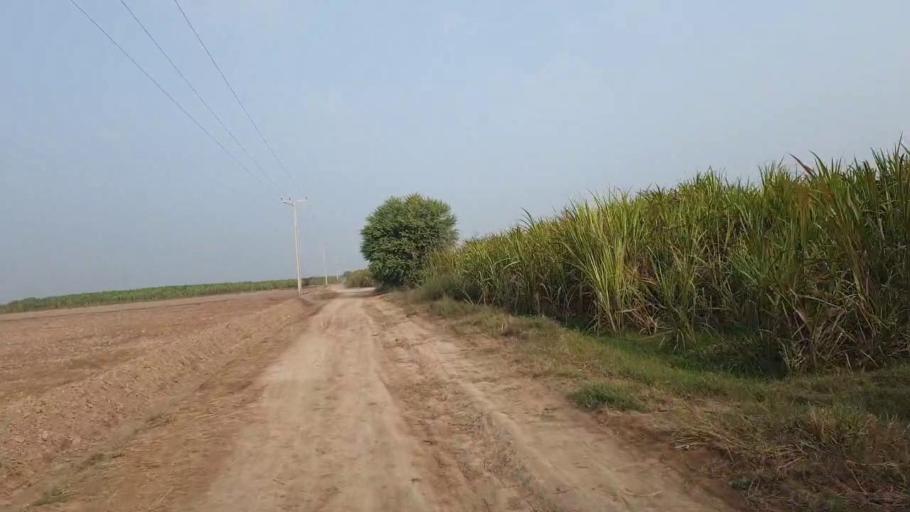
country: PK
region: Sindh
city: Tando Muhammad Khan
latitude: 25.1468
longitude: 68.5896
